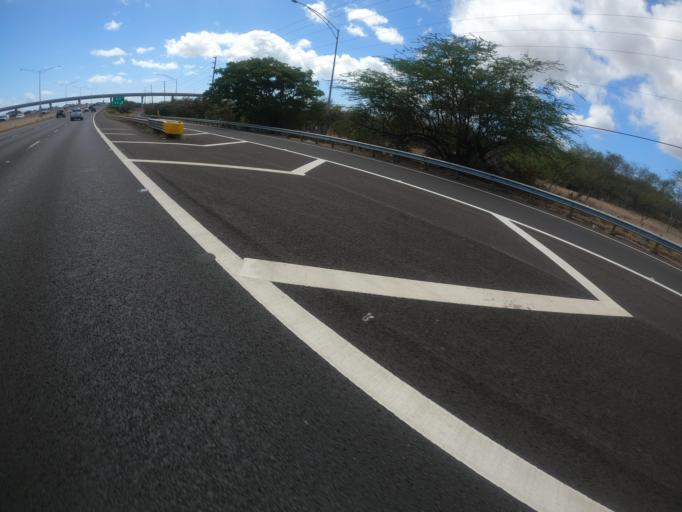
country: US
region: Hawaii
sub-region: Honolulu County
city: Royal Kunia
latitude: 21.3788
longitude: -158.0283
